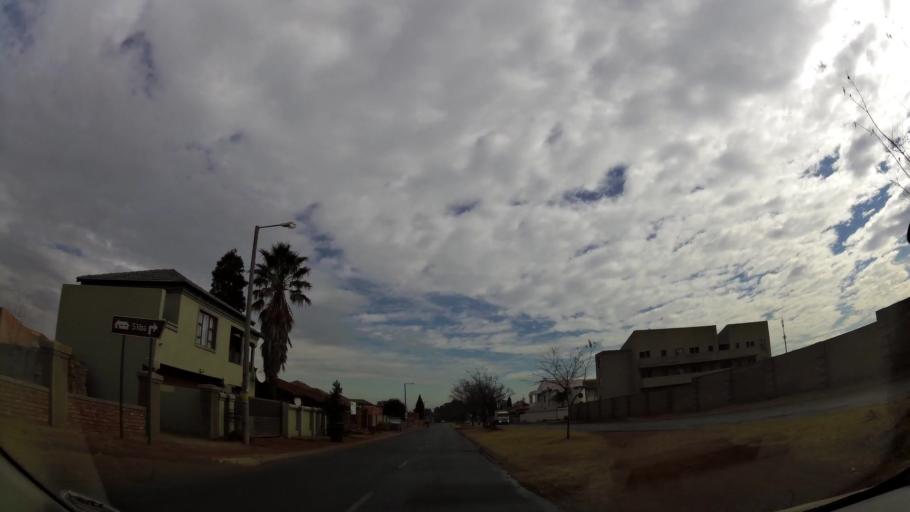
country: ZA
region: Gauteng
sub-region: Ekurhuleni Metropolitan Municipality
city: Germiston
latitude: -26.3203
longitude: 28.1810
